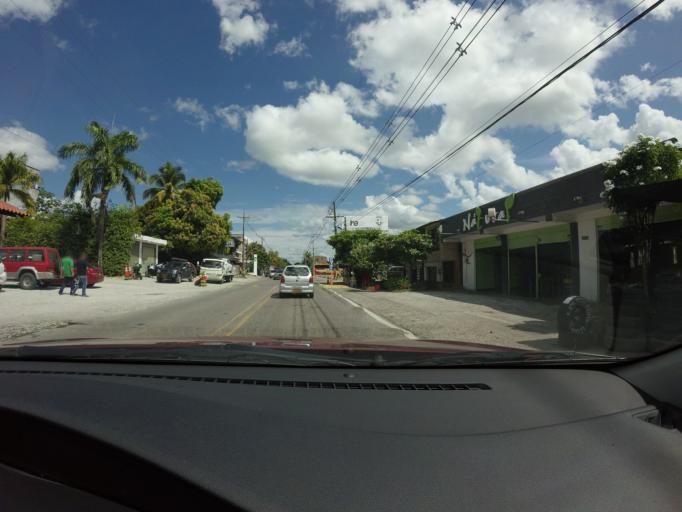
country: CO
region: Antioquia
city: Puerto Triunfo
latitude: 5.8982
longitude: -74.7379
